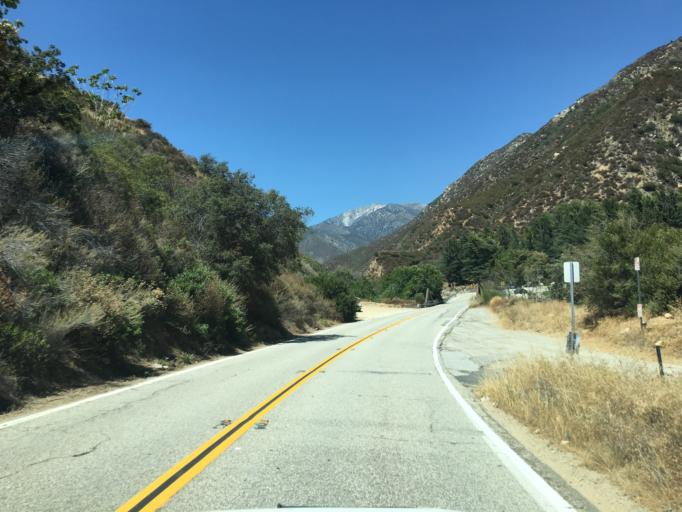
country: US
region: California
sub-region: San Bernardino County
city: San Antonio Heights
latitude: 34.1767
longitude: -117.6760
